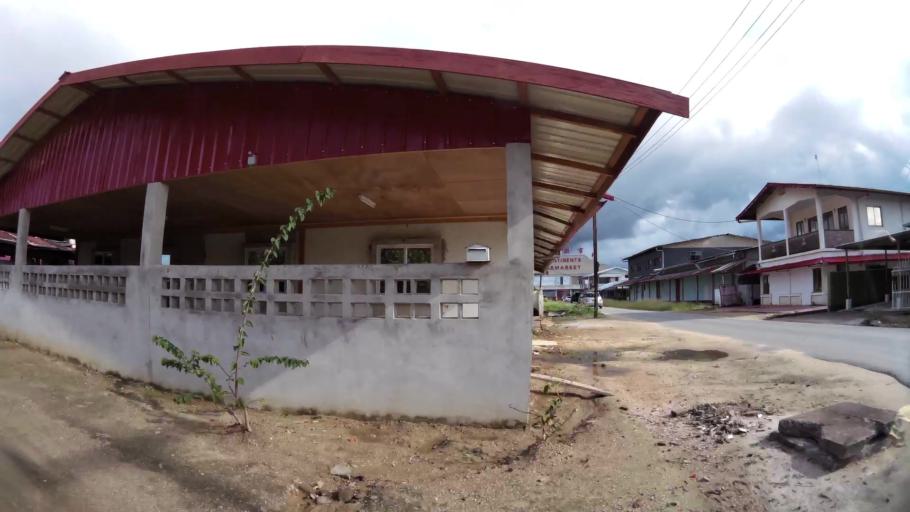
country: SR
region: Paramaribo
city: Paramaribo
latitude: 5.8441
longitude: -55.2129
